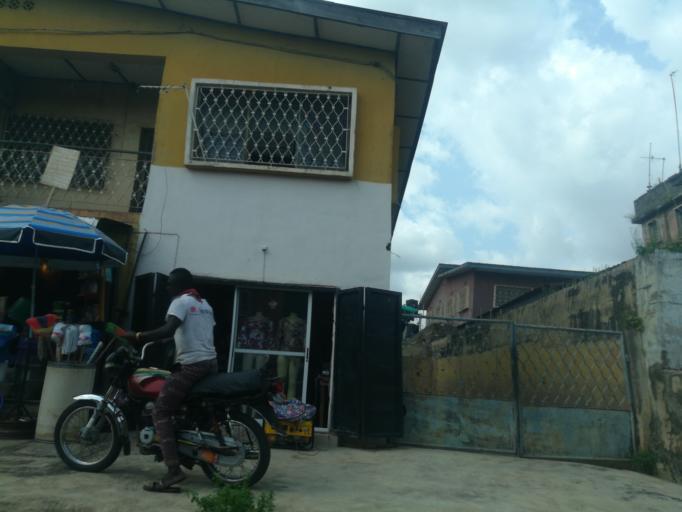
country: NG
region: Oyo
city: Ibadan
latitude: 7.3630
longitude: 3.8739
